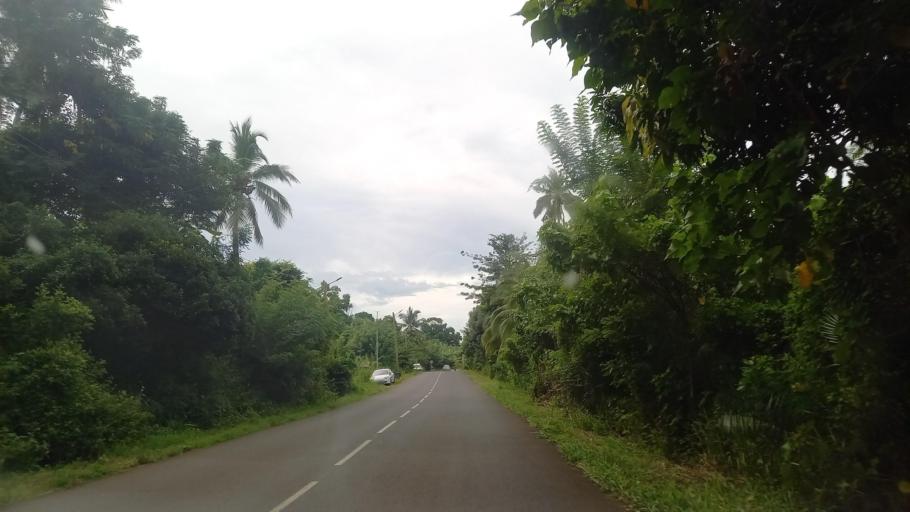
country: YT
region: Boueni
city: Boueni
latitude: -12.9087
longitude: 45.1011
